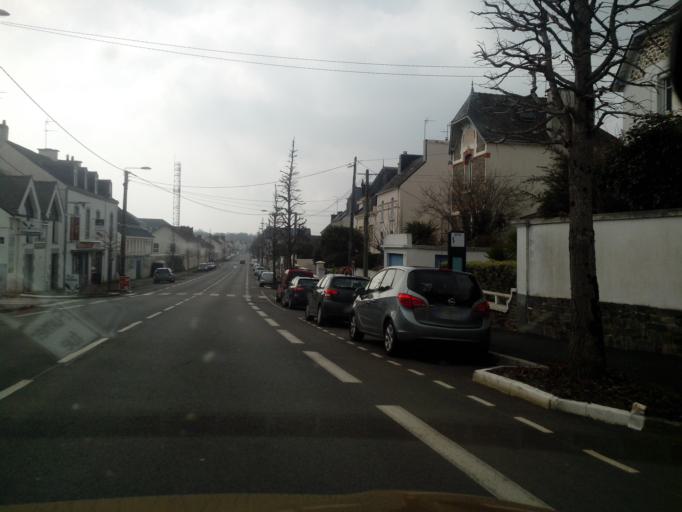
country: FR
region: Brittany
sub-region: Departement du Morbihan
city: Vannes
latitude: 47.6621
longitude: -2.7402
